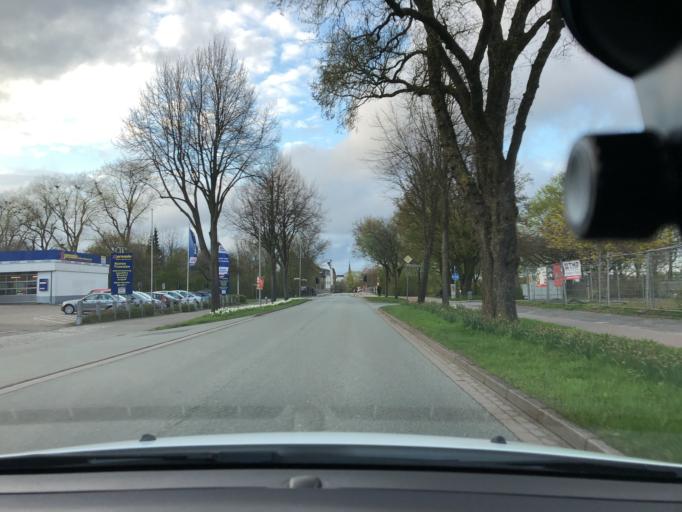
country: DE
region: Schleswig-Holstein
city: Flensburg
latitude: 54.7728
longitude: 9.4352
